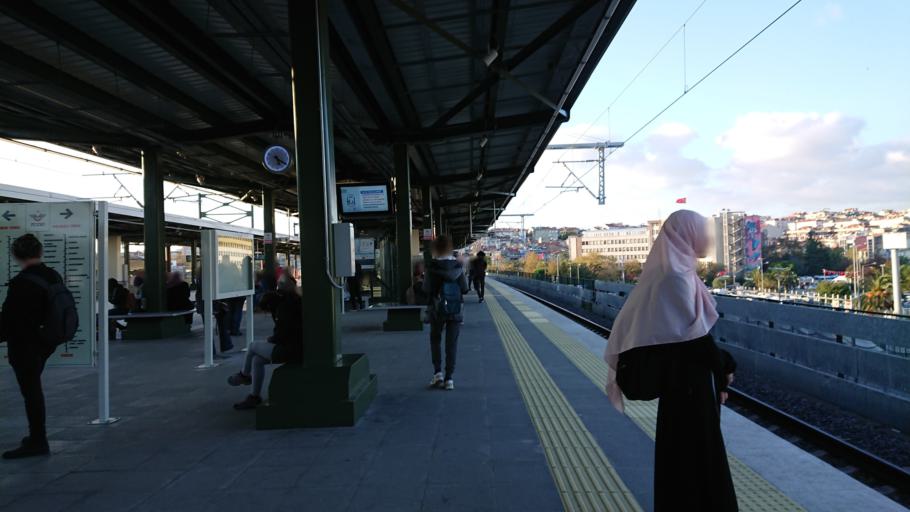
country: TR
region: Istanbul
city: UEskuedar
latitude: 40.9904
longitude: 29.0383
